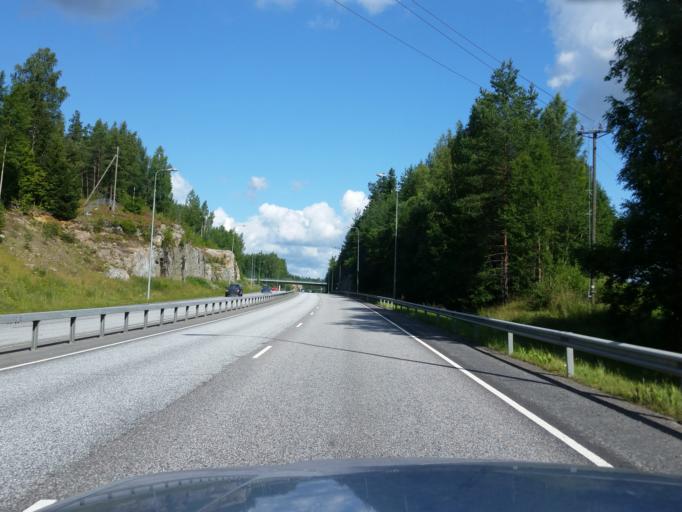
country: FI
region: Uusimaa
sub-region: Helsinki
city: Vihti
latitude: 60.3204
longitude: 24.3429
